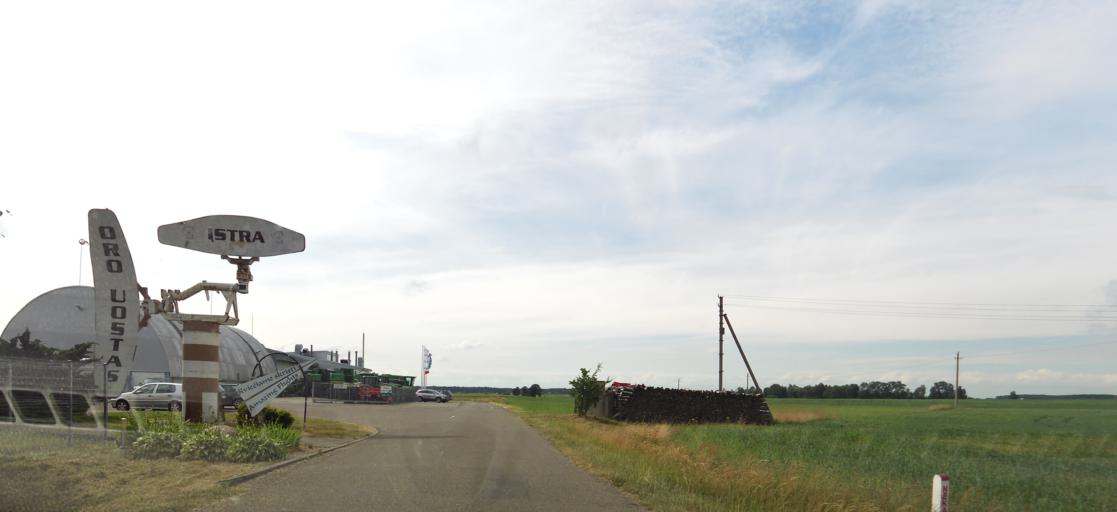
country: LT
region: Panevezys
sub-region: Panevezys City
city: Panevezys
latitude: 55.8285
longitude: 24.3608
